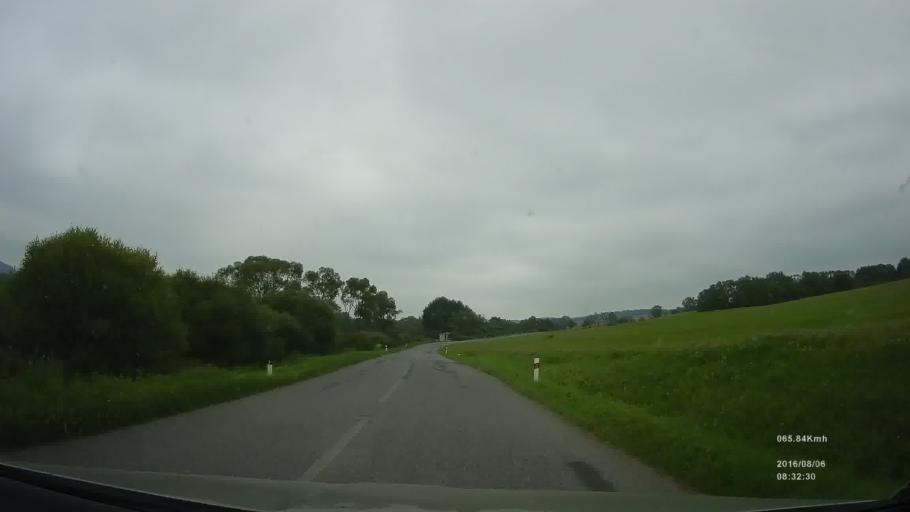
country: SK
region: Presovsky
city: Svidnik
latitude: 49.3359
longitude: 21.5963
